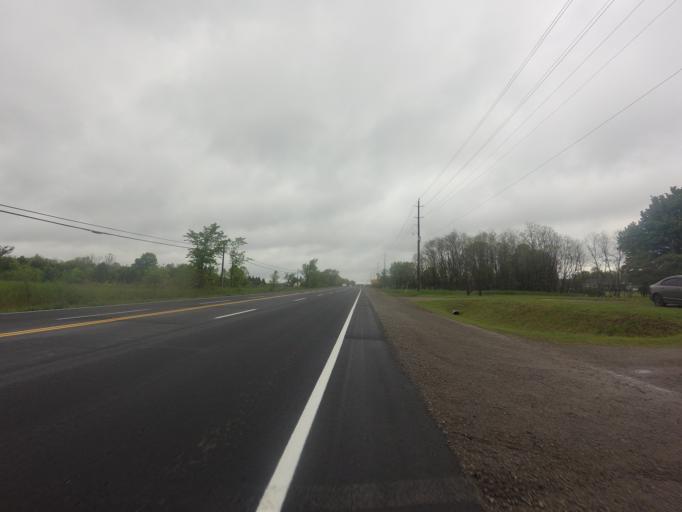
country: CA
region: Ontario
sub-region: Lanark County
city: Smiths Falls
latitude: 44.8057
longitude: -76.0946
